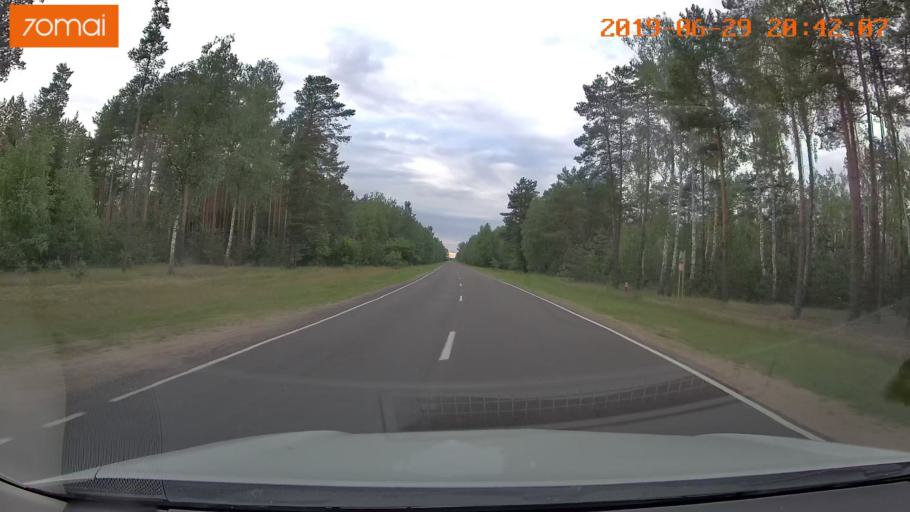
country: BY
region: Brest
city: Hantsavichy
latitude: 52.5940
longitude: 26.3306
